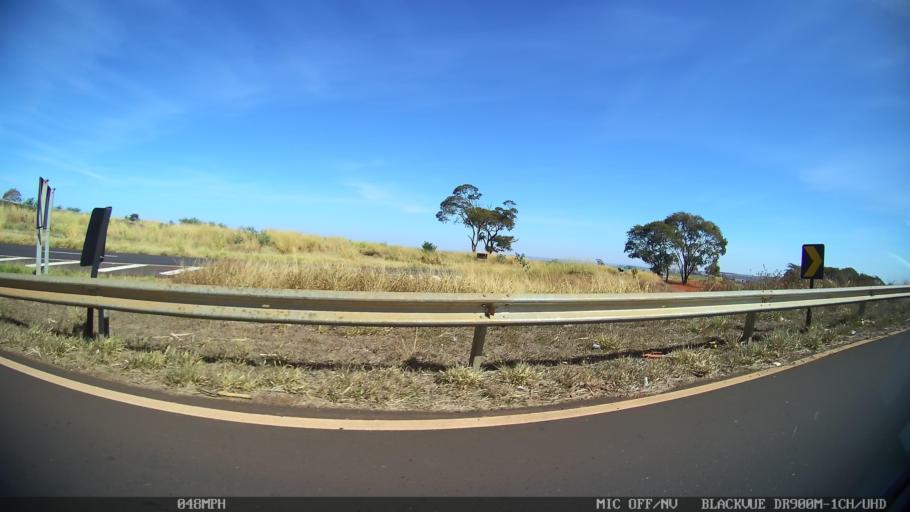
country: BR
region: Sao Paulo
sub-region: Nuporanga
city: Nuporanga
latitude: -20.5604
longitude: -47.6256
